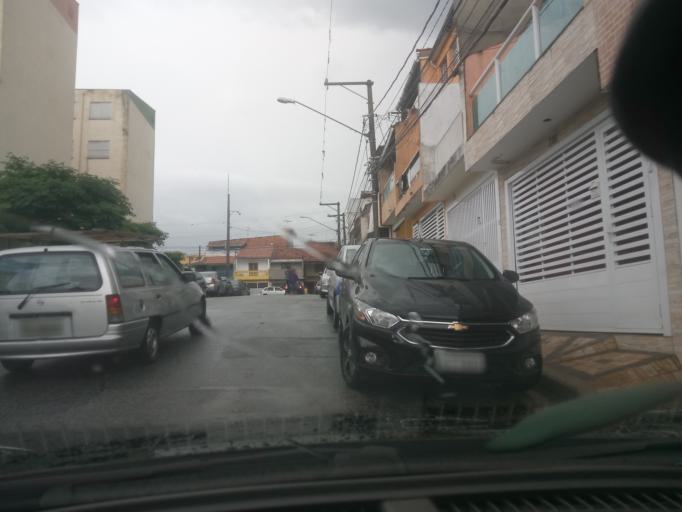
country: BR
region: Sao Paulo
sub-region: Sao Bernardo Do Campo
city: Sao Bernardo do Campo
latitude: -23.7021
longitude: -46.5574
